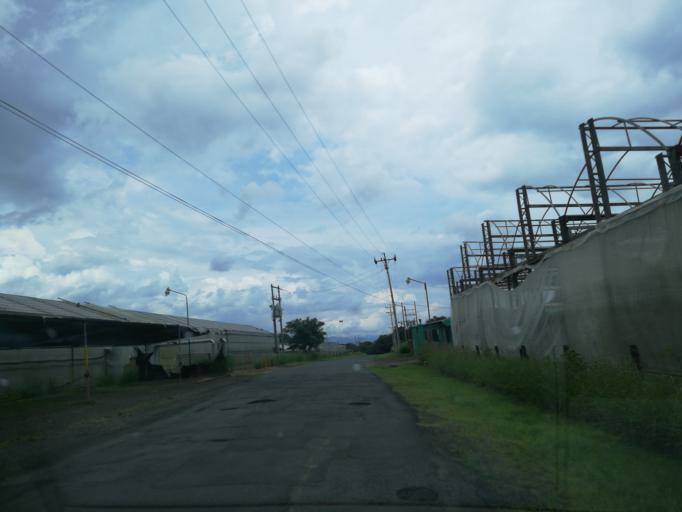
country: CR
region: Alajuela
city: Alajuela
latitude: 10.0336
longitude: -84.1911
